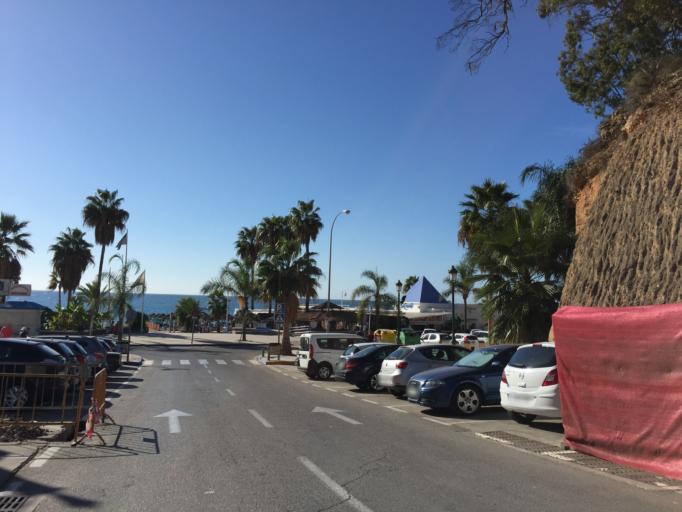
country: ES
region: Andalusia
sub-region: Provincia de Malaga
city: Nerja
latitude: 36.7503
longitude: -3.8693
